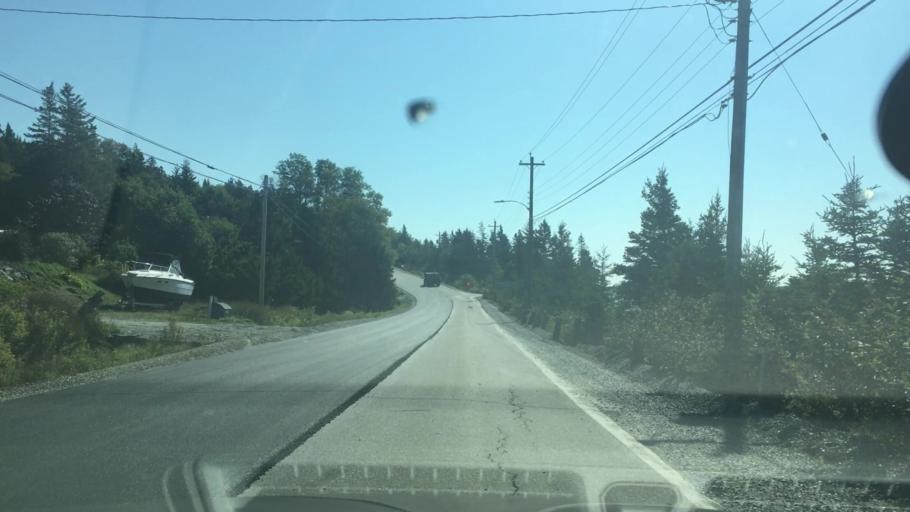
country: CA
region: Nova Scotia
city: New Glasgow
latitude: 44.9114
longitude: -62.5067
